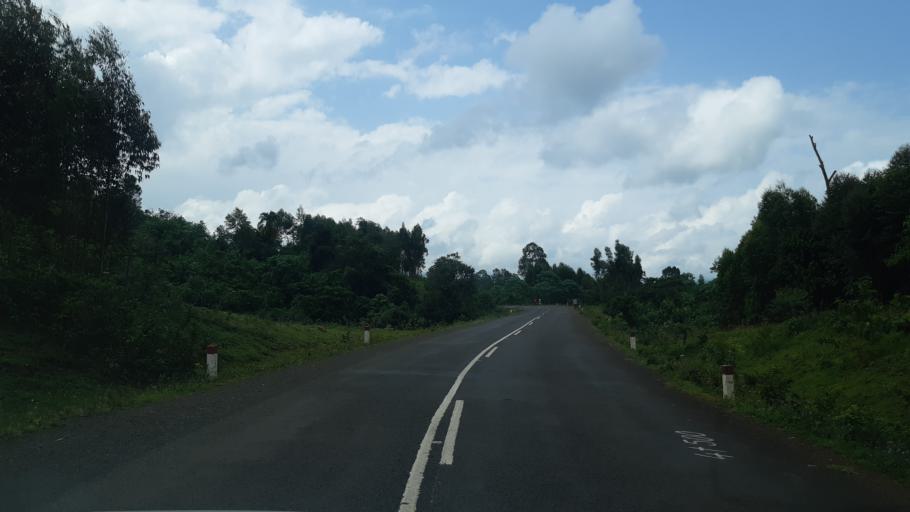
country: ET
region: Southern Nations, Nationalities, and People's Region
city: Bonga
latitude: 7.2364
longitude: 36.2624
